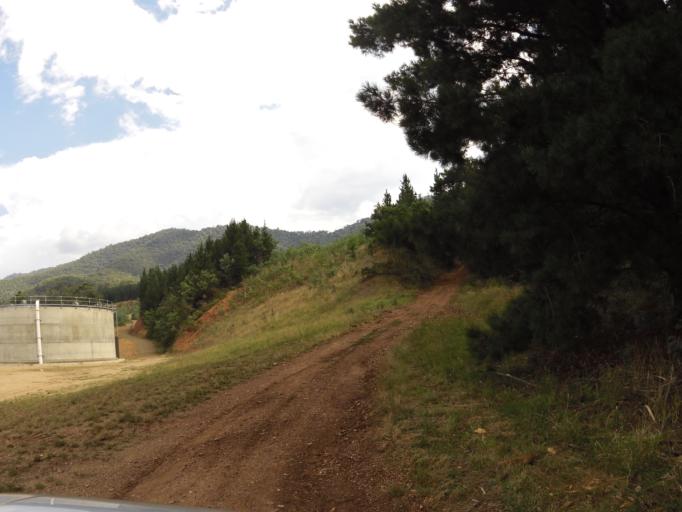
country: AU
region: Victoria
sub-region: Alpine
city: Mount Beauty
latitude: -36.7639
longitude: 147.0199
